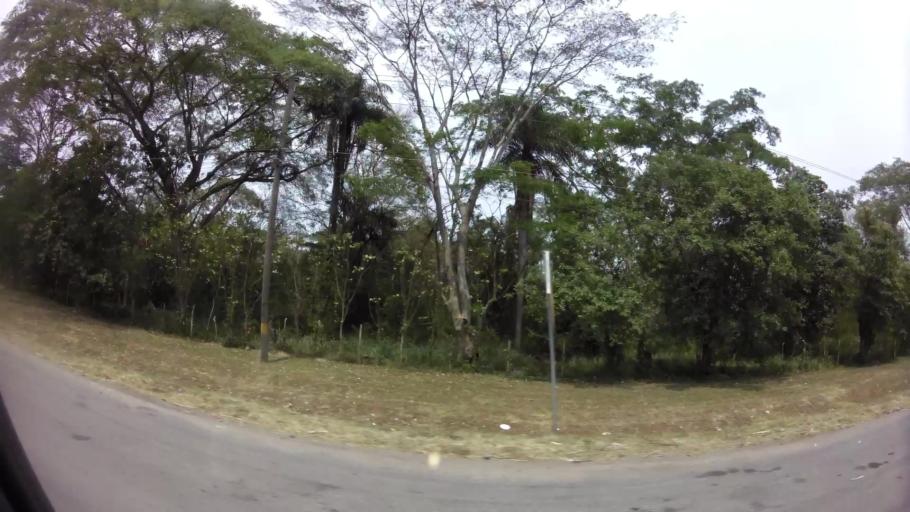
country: HN
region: Cortes
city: Nuevo Chamelecon
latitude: 15.3692
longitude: -87.9856
